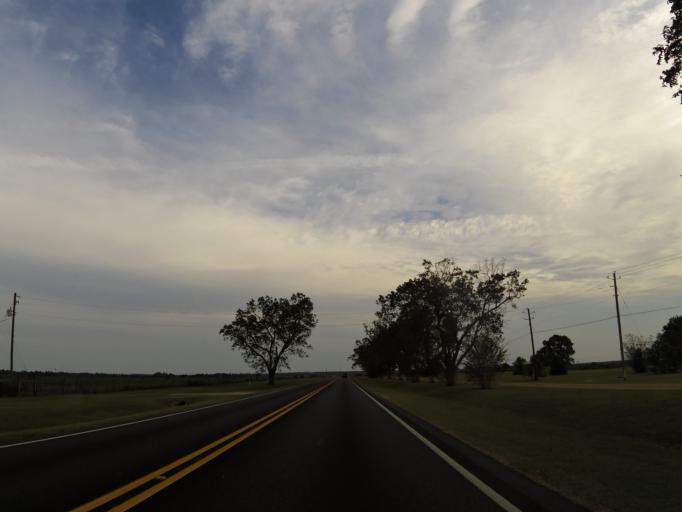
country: US
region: Alabama
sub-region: Escambia County
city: Atmore
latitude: 31.1533
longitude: -87.4636
